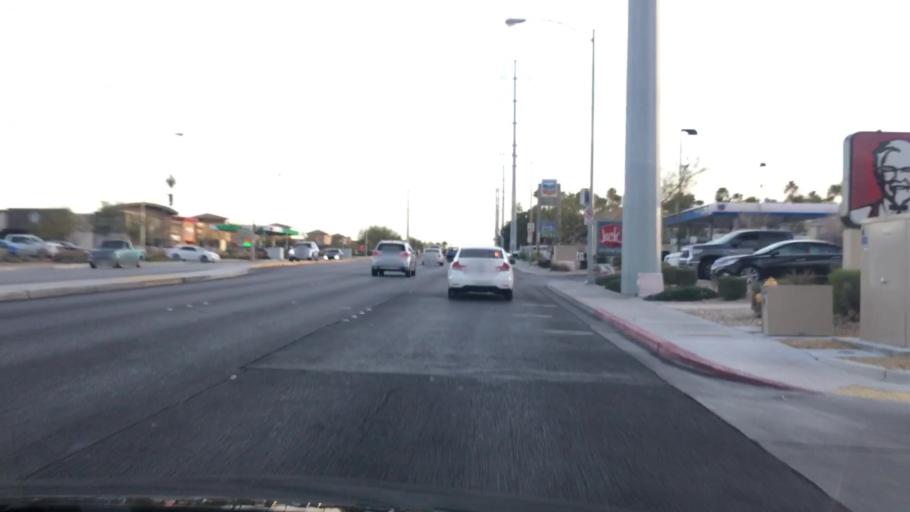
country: US
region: Nevada
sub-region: Clark County
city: Enterprise
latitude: 36.0605
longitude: -115.2794
